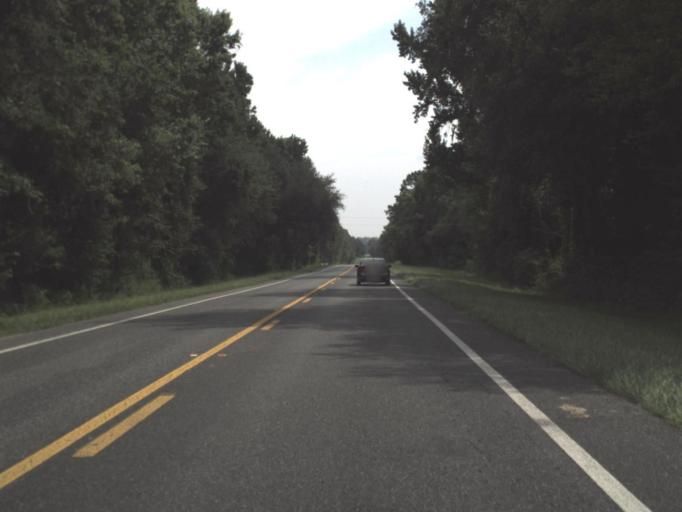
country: US
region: Florida
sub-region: Alachua County
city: High Springs
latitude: 29.9748
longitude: -82.6001
